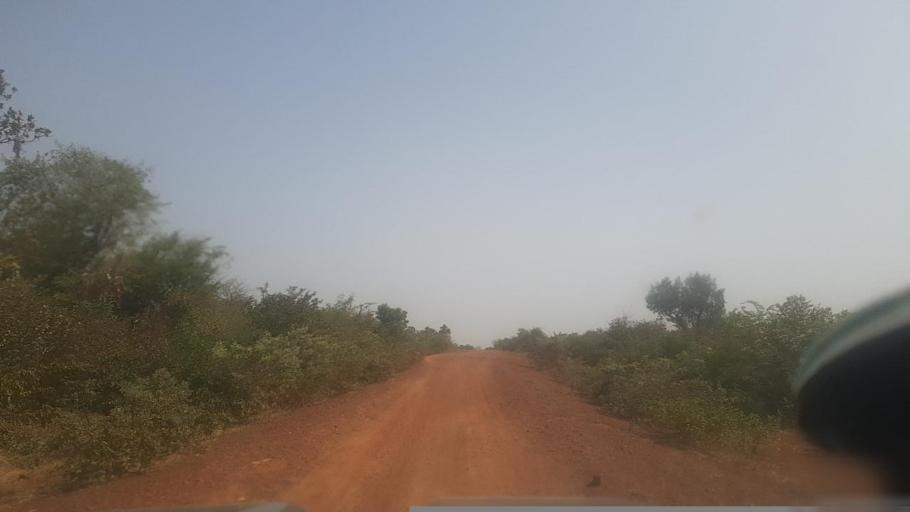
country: ML
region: Segou
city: Segou
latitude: 12.9295
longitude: -6.2790
